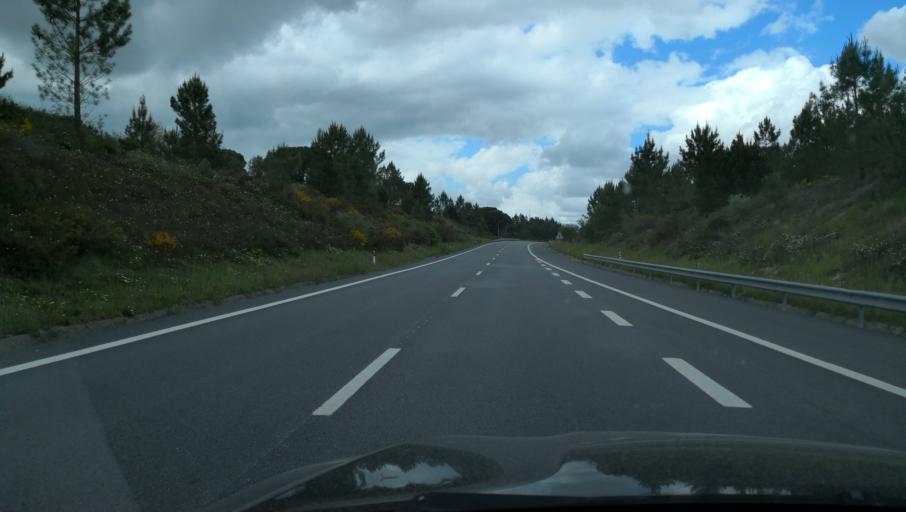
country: PT
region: Evora
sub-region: Vendas Novas
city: Vendas Novas
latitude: 38.6054
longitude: -8.6454
